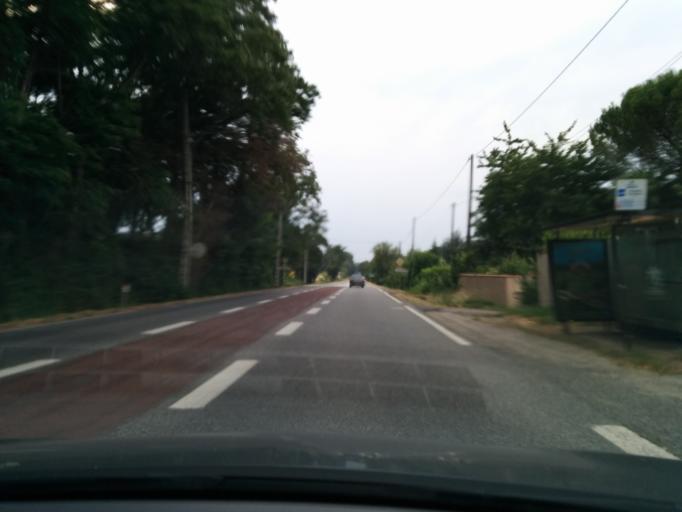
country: FR
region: Midi-Pyrenees
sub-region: Departement de la Haute-Garonne
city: Montgiscard
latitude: 43.4651
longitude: 1.5655
